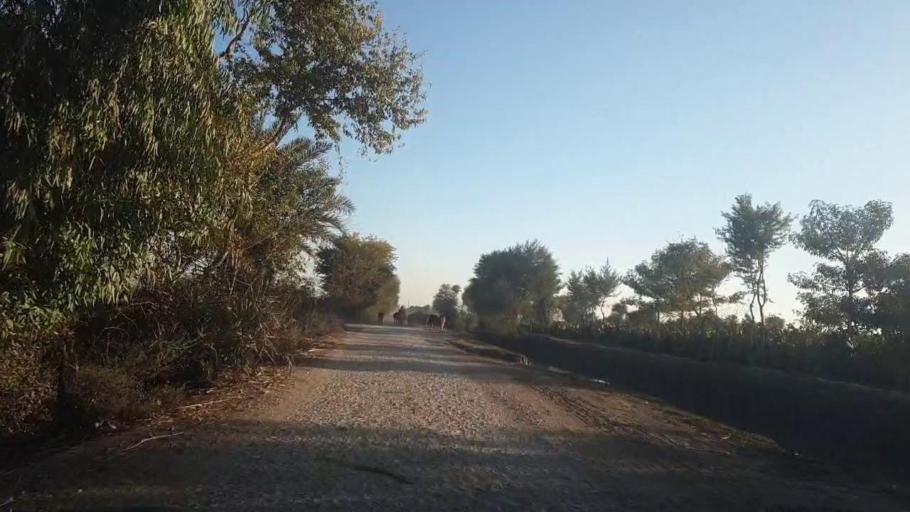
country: PK
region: Sindh
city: Ghotki
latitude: 28.0070
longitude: 69.2696
